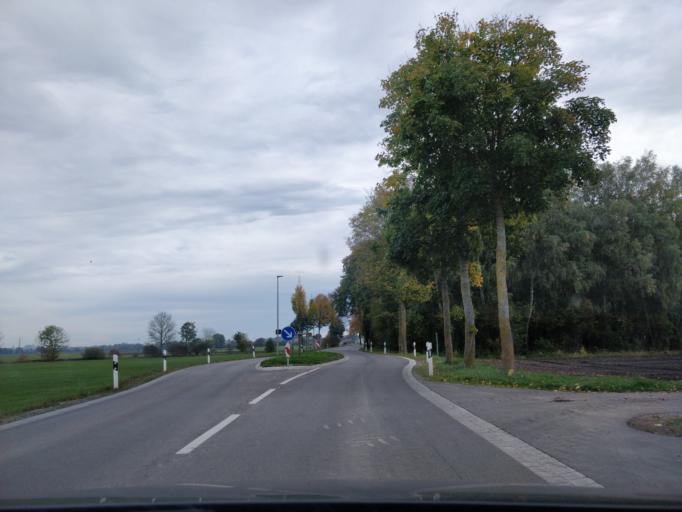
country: DE
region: Bavaria
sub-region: Swabia
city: Wiedergeltingen
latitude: 48.0377
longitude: 10.6797
